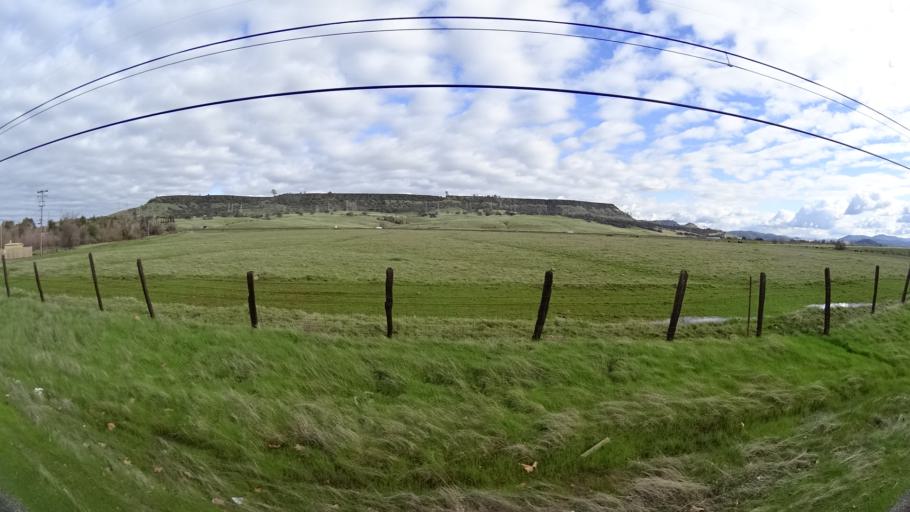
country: US
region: California
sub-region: Butte County
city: Thermalito
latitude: 39.5340
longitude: -121.5747
